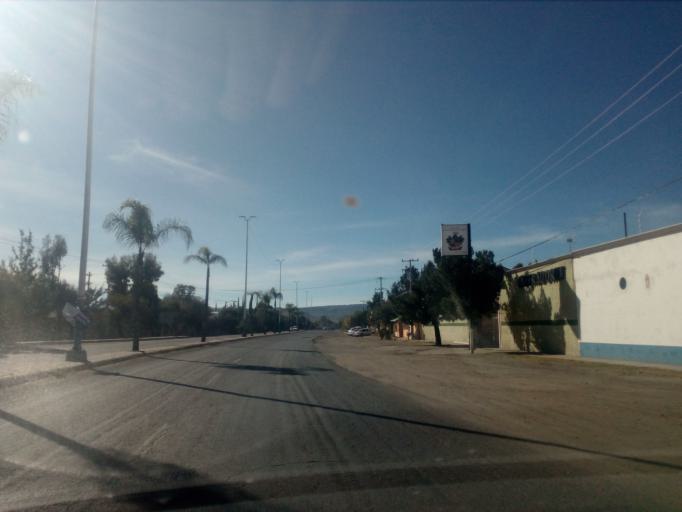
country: MX
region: Durango
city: Victoria de Durango
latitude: 23.9823
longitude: -104.6643
